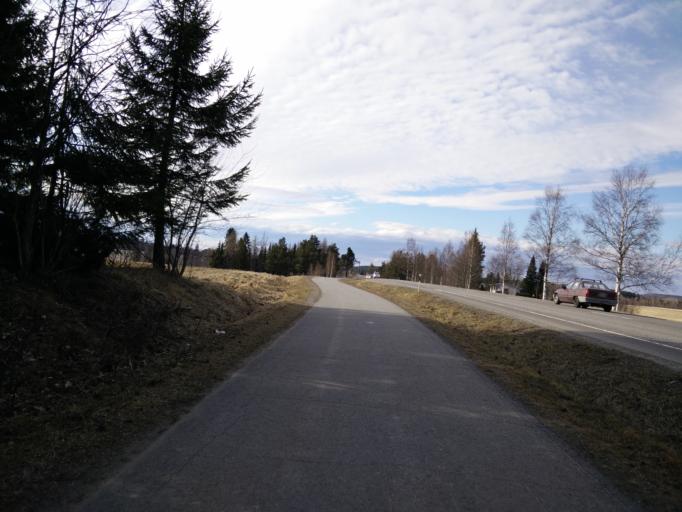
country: FI
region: Pirkanmaa
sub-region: Tampere
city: Orivesi
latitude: 61.7039
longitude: 24.3382
